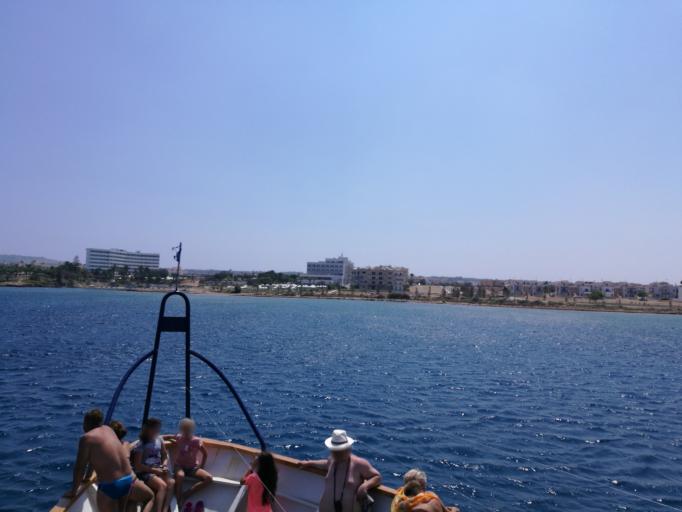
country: CY
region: Ammochostos
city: Protaras
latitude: 35.0479
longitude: 34.0329
